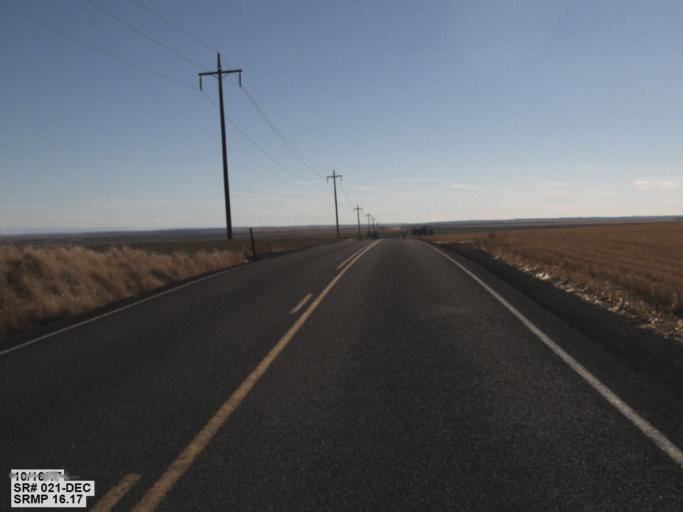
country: US
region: Washington
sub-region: Adams County
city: Ritzville
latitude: 46.8604
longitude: -118.5468
